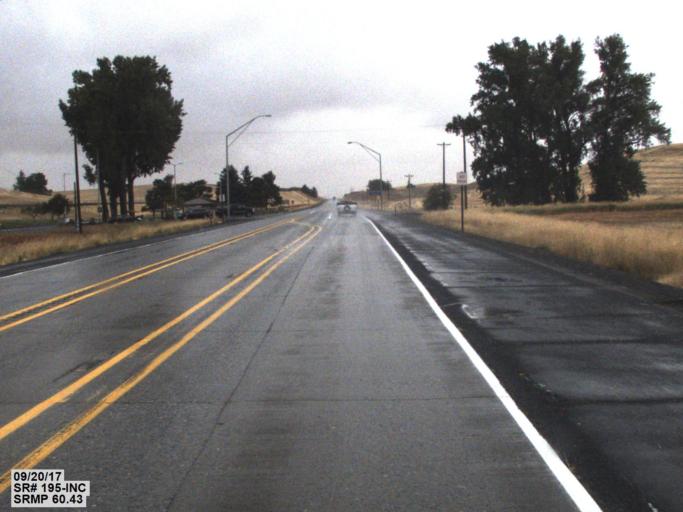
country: US
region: Washington
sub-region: Whitman County
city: Colfax
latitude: 47.1807
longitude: -117.3774
